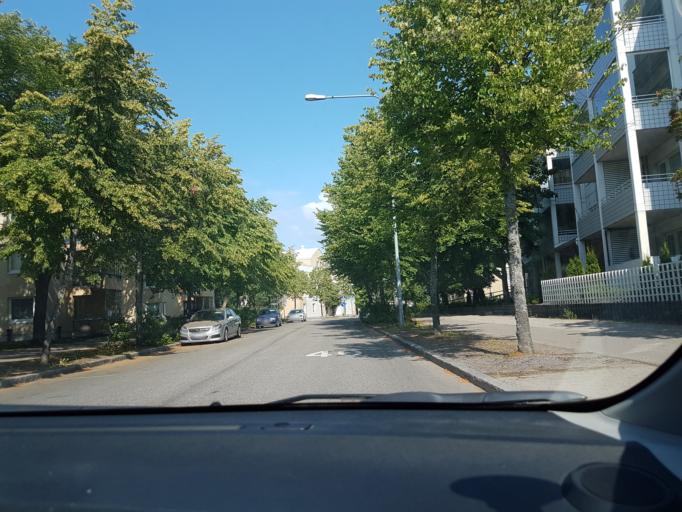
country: FI
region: Uusimaa
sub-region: Helsinki
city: Vantaa
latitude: 60.2023
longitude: 25.1280
